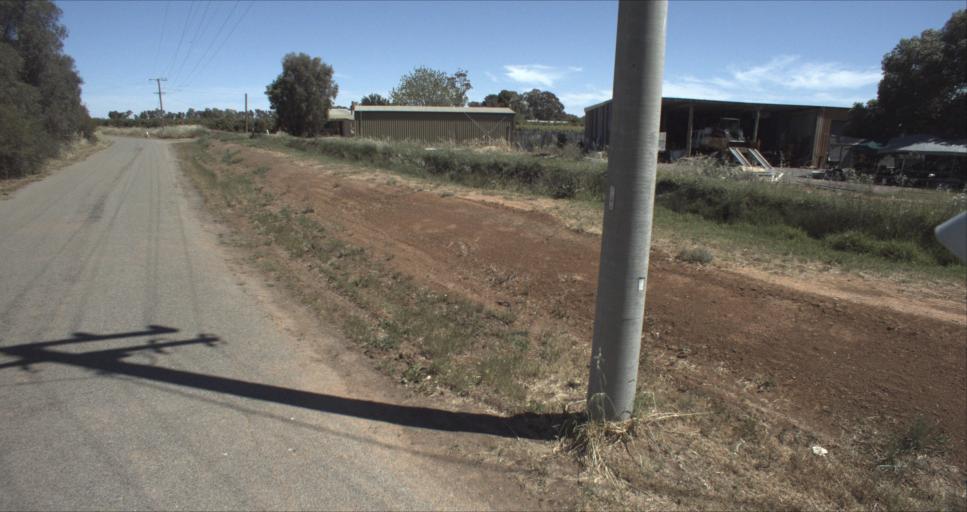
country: AU
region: New South Wales
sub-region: Leeton
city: Leeton
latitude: -34.5268
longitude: 146.3461
